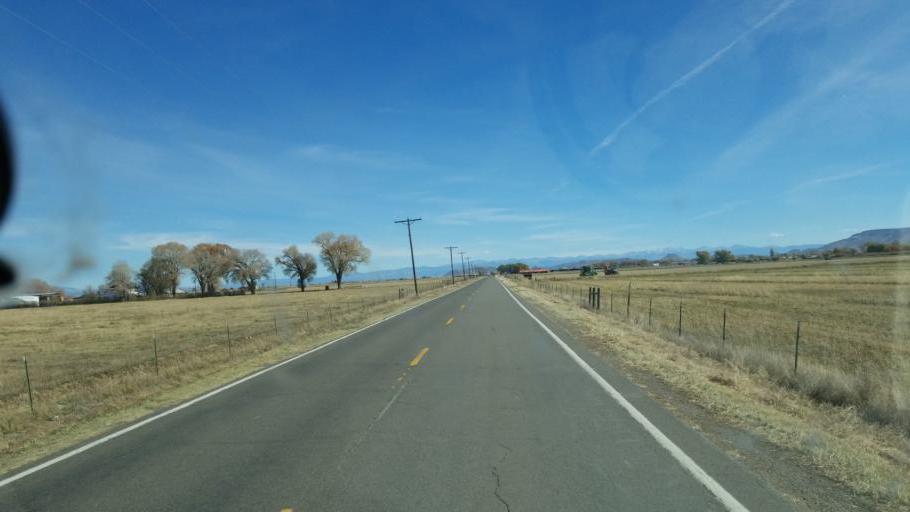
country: US
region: Colorado
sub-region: Conejos County
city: Conejos
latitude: 37.2836
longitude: -105.9723
